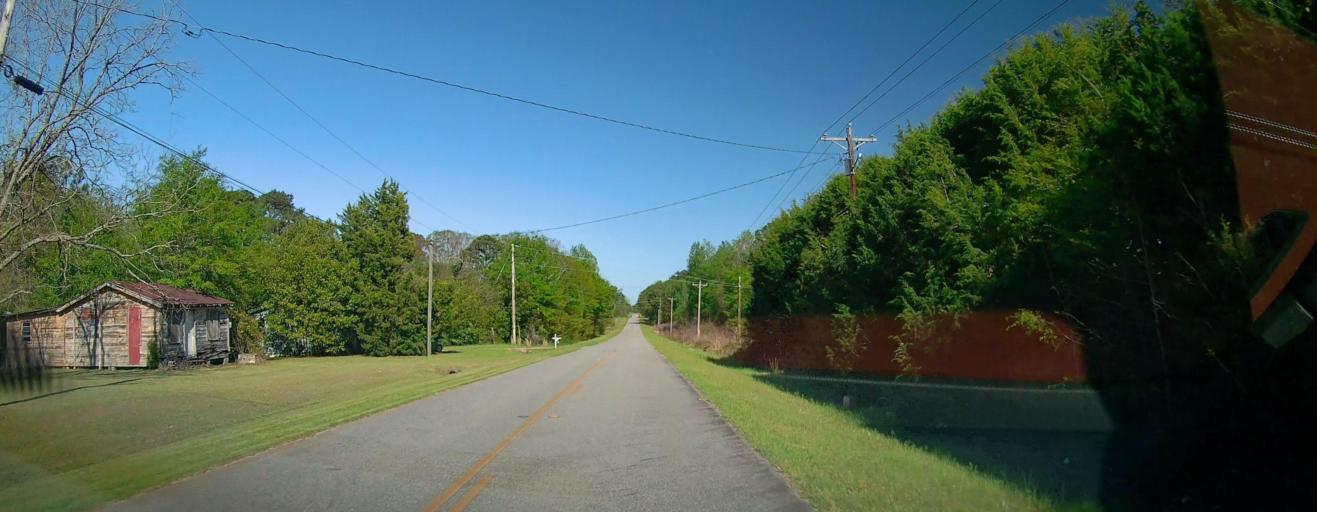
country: US
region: Georgia
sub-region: Pulaski County
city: Hawkinsville
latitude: 32.2477
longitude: -83.4836
